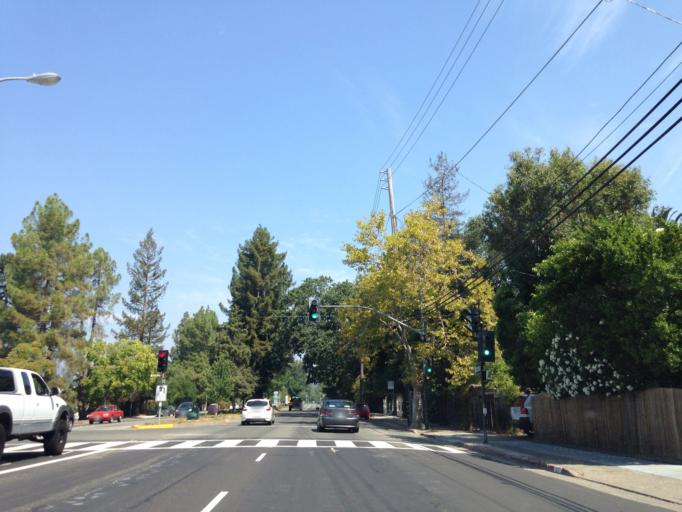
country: US
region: California
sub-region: Marin County
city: San Anselmo
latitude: 37.9693
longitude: -122.5604
